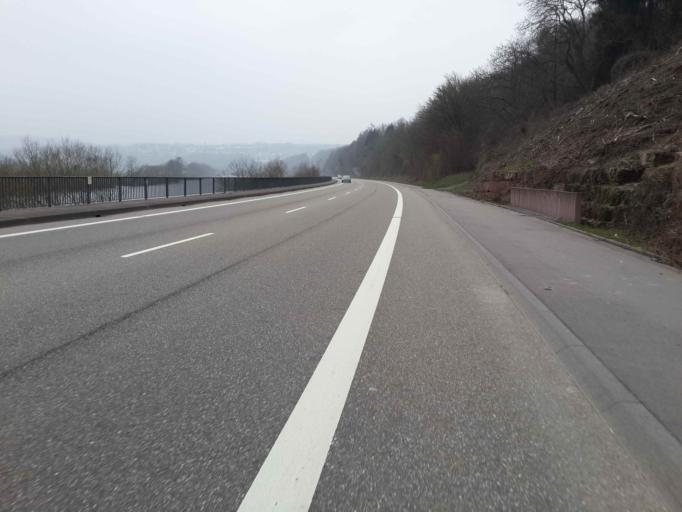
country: DE
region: Baden-Wuerttemberg
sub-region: Karlsruhe Region
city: Obrigheim
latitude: 49.3606
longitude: 9.1029
